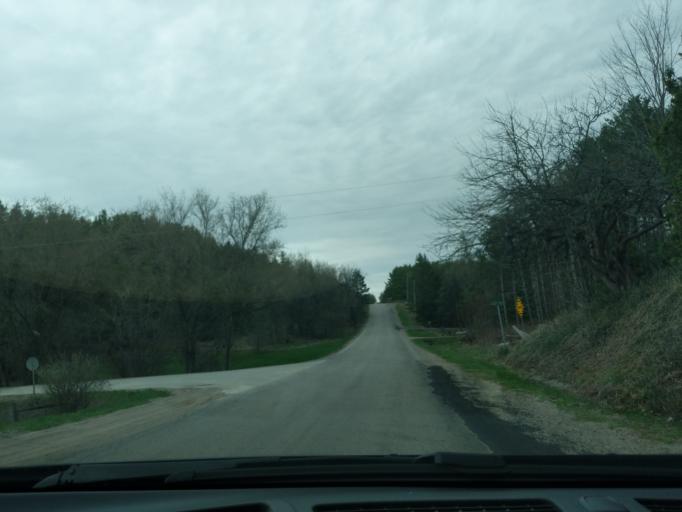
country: CA
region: Ontario
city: Orangeville
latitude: 44.0059
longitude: -79.9651
